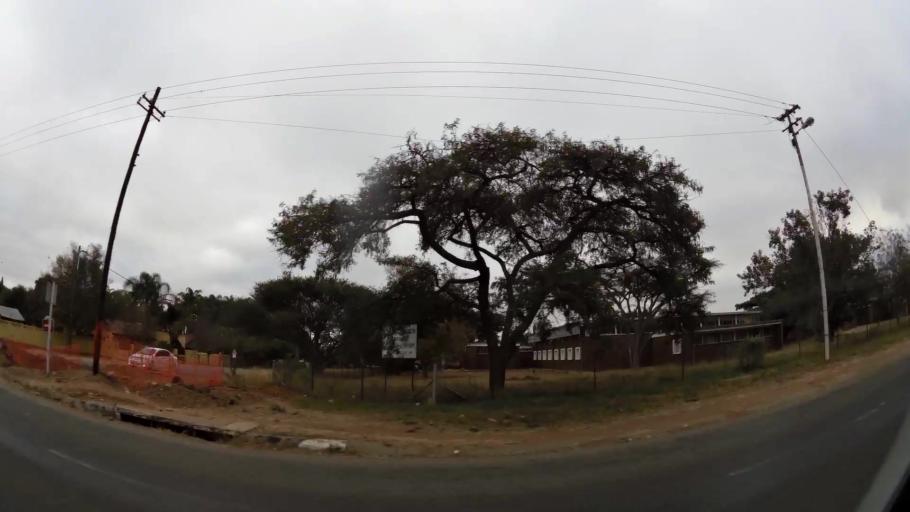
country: ZA
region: Limpopo
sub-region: Capricorn District Municipality
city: Polokwane
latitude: -23.8991
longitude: 29.4685
